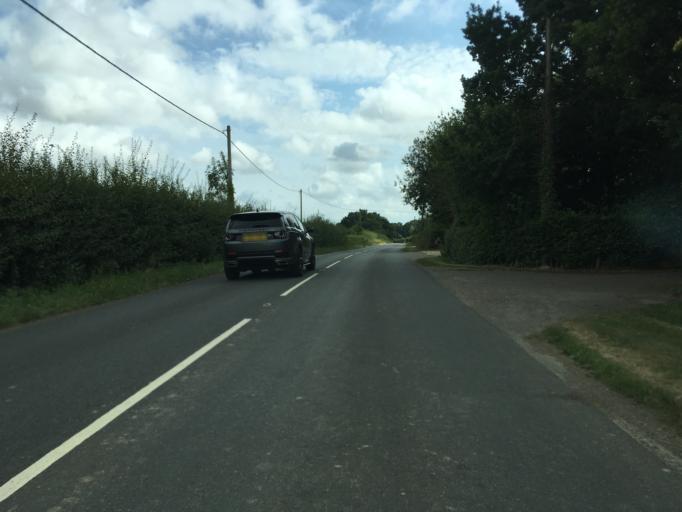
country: GB
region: England
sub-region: Kent
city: Tenterden
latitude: 51.0564
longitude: 0.7297
